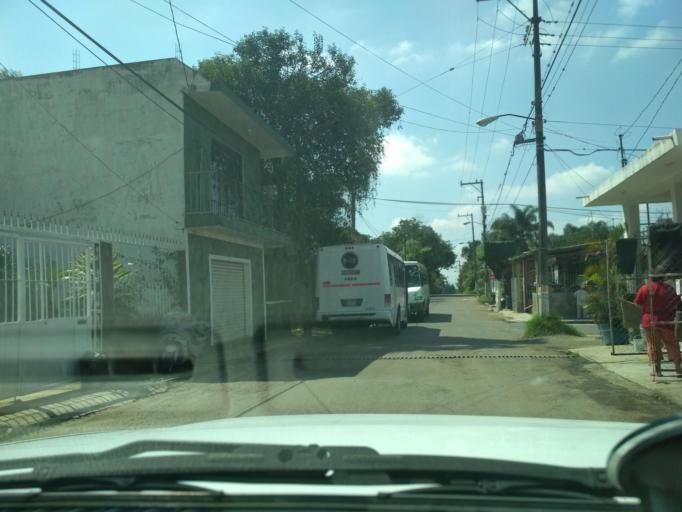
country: MX
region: Veracruz
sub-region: Fortin
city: Cordoba (Santa Leticia)
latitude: 18.9145
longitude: -96.9731
